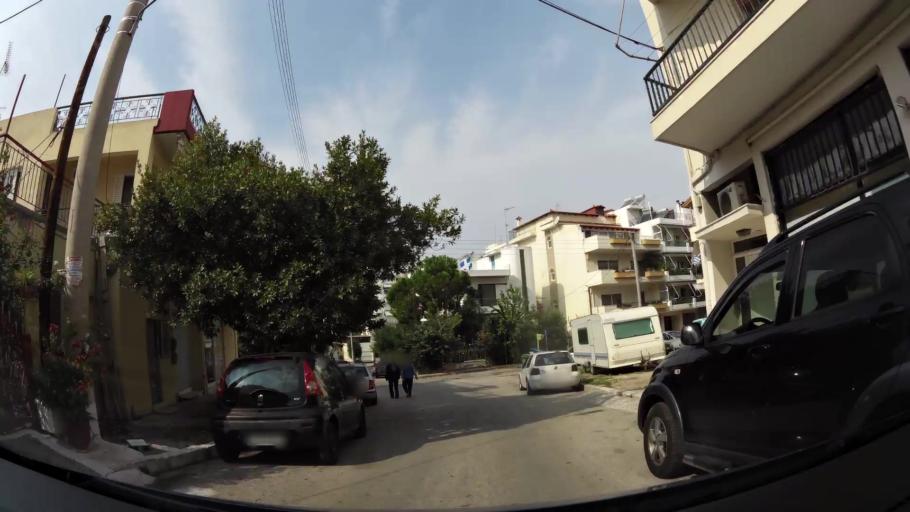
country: GR
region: Attica
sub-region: Nomarchia Athinas
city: Agios Dimitrios
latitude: 37.9287
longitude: 23.7291
